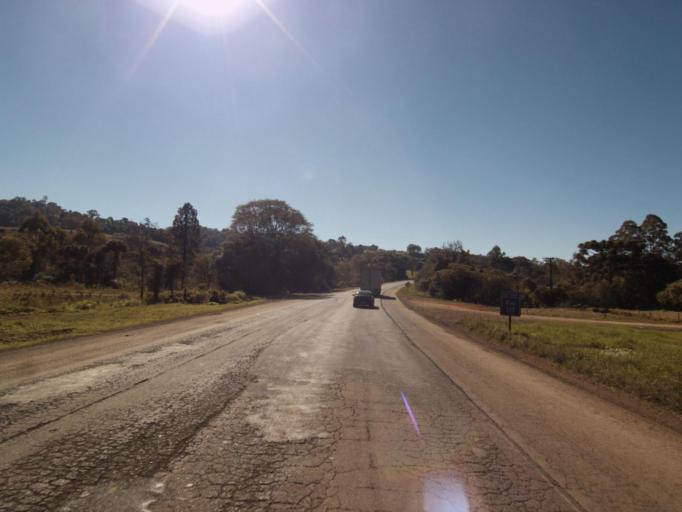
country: BR
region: Rio Grande do Sul
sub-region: Frederico Westphalen
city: Frederico Westphalen
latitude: -26.8959
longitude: -53.1903
